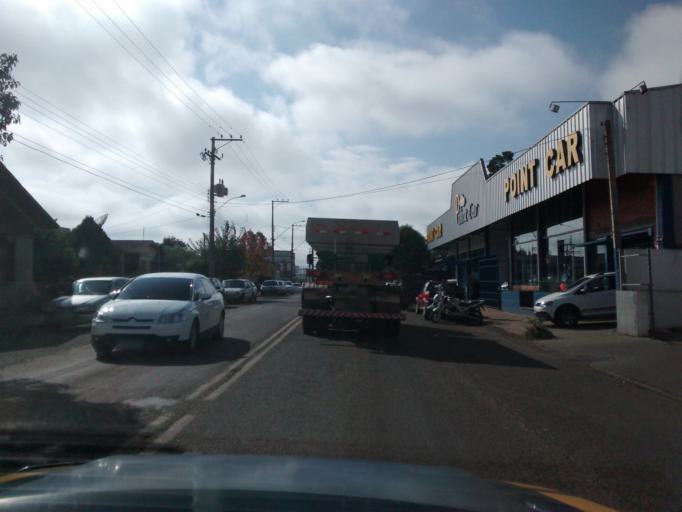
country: BR
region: Rio Grande do Sul
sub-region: Vacaria
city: Vacaria
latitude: -28.5099
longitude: -50.9325
